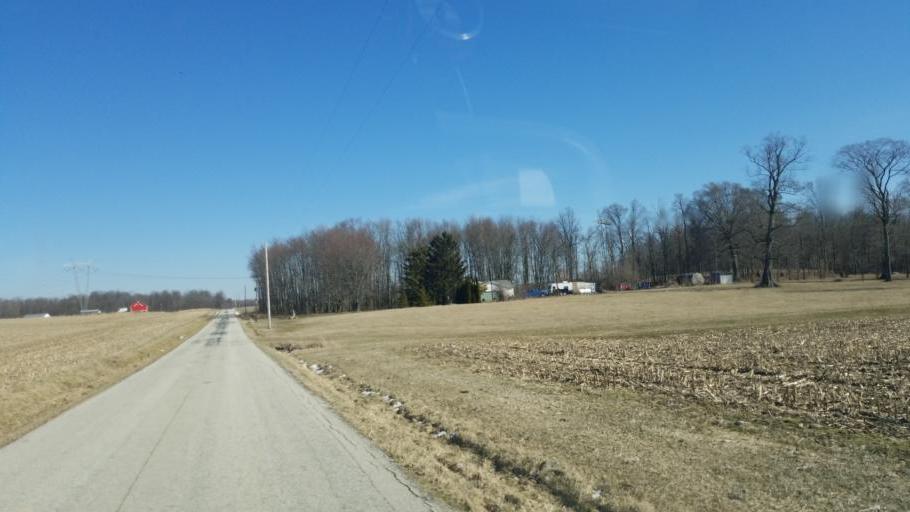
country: US
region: Ohio
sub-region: Crawford County
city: Galion
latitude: 40.6294
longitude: -82.7091
